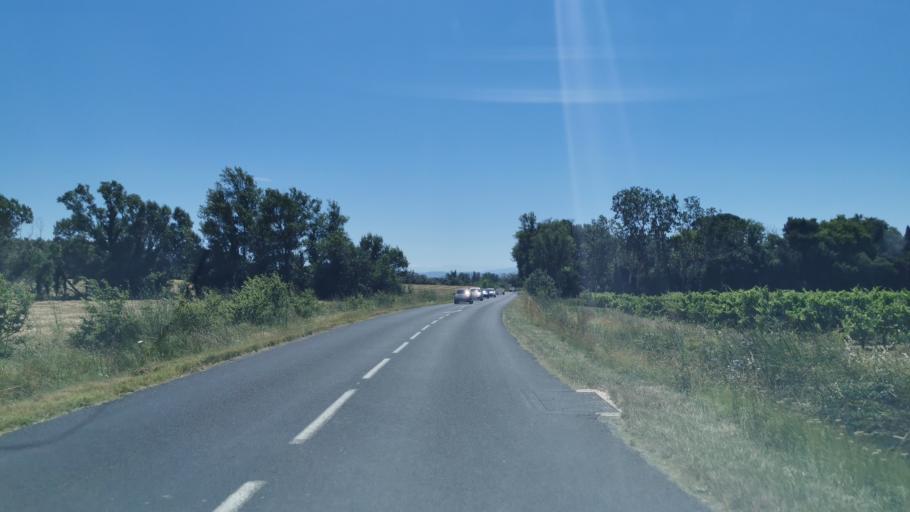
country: FR
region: Languedoc-Roussillon
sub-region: Departement de l'Aude
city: Vinassan
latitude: 43.2326
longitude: 3.0980
